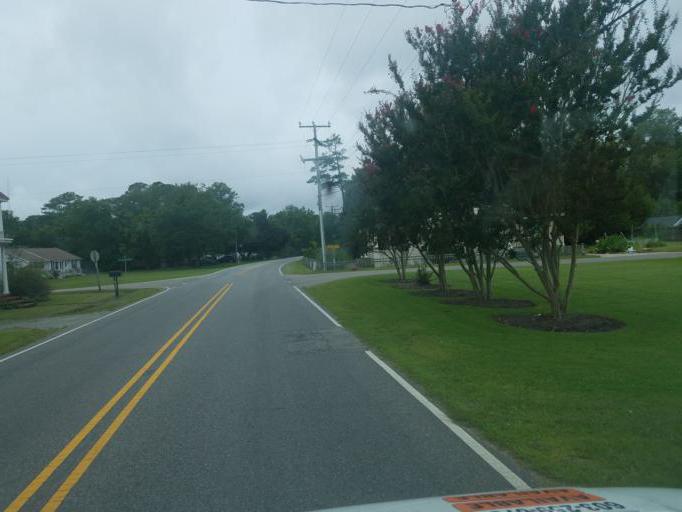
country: US
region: North Carolina
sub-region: Dare County
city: Wanchese
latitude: 35.8448
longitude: -75.6356
